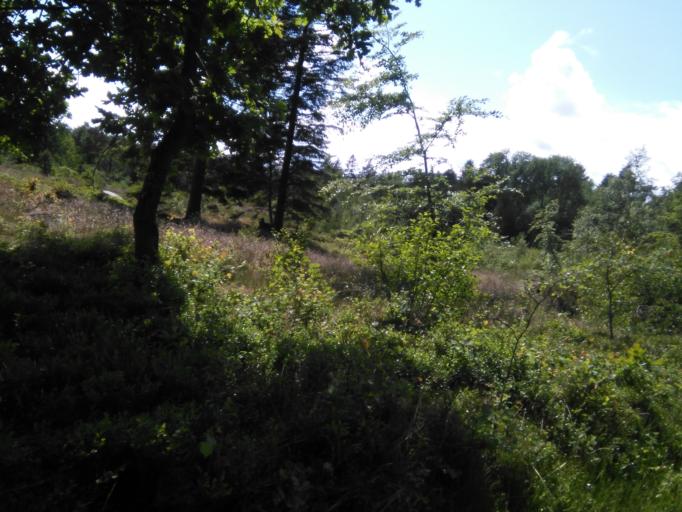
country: DK
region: Capital Region
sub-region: Bornholm Kommune
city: Nexo
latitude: 55.0934
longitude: 15.1041
